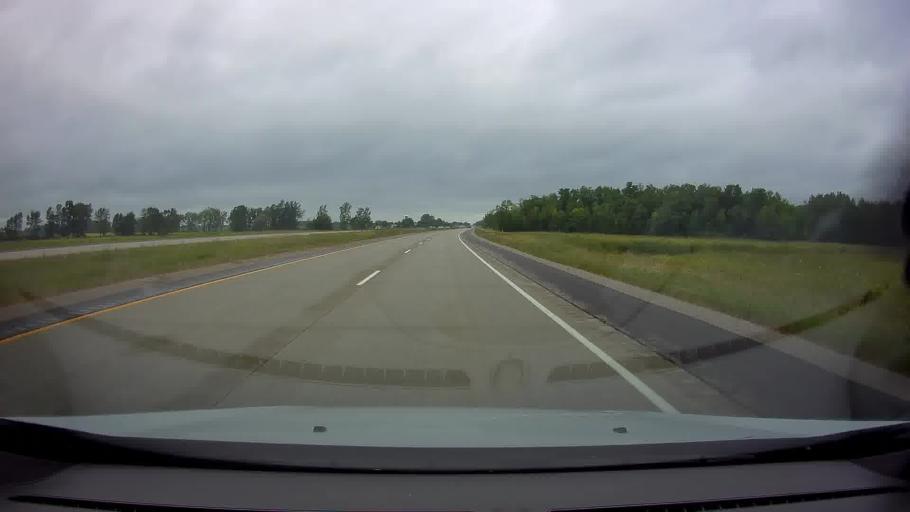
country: US
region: Wisconsin
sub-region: Brown County
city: Pulaski
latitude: 44.6156
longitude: -88.2653
